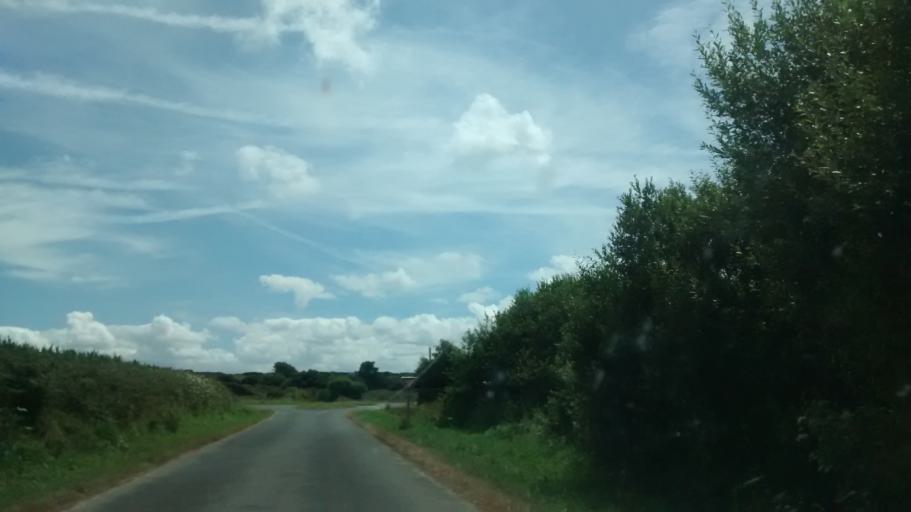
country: FR
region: Brittany
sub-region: Departement du Finistere
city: Plouguerneau
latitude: 48.6196
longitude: -4.4700
